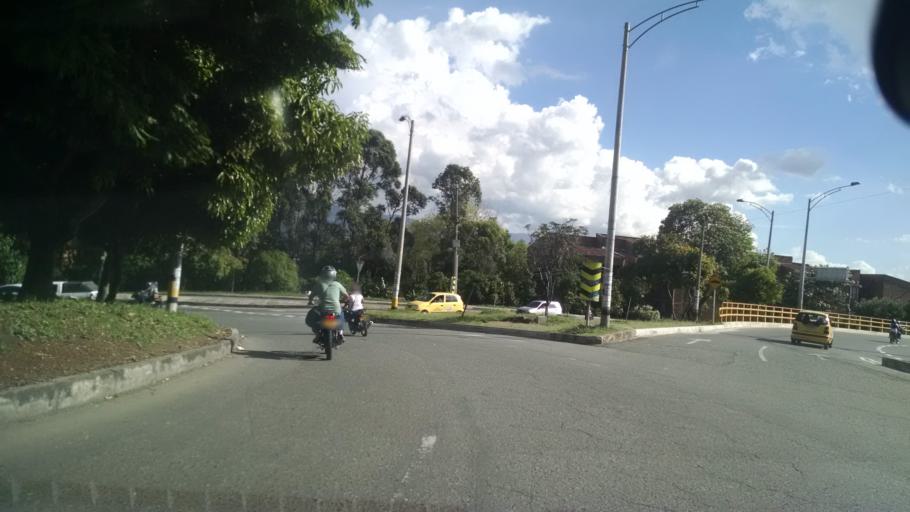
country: CO
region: Antioquia
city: Medellin
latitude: 6.2836
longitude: -75.5840
